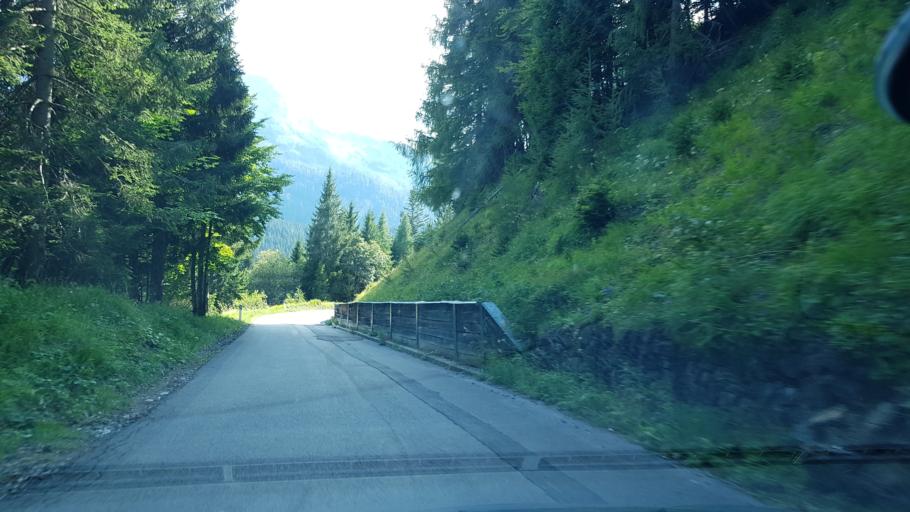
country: IT
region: Friuli Venezia Giulia
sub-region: Provincia di Udine
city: Sauris di Sotto
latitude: 46.4721
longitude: 12.6524
